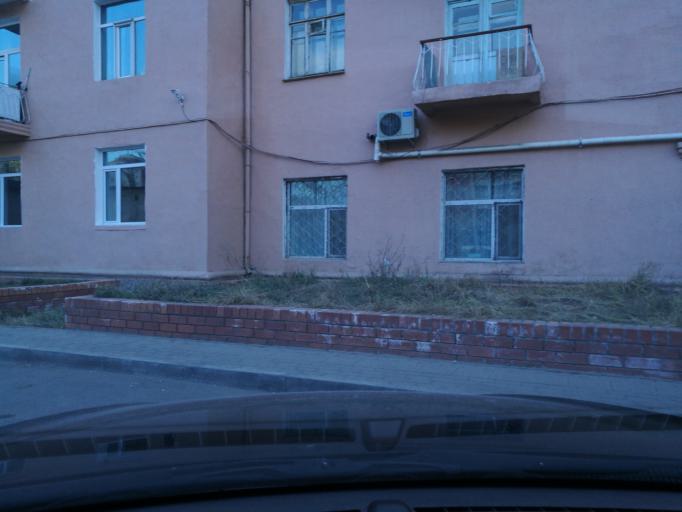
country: MN
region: Ulaanbaatar
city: Ulaanbaatar
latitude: 47.9255
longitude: 106.9185
